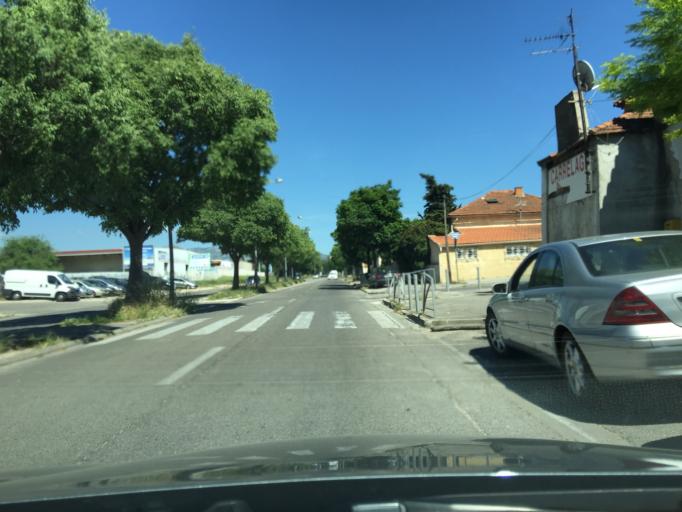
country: FR
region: Provence-Alpes-Cote d'Azur
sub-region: Departement des Bouches-du-Rhone
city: La Penne-sur-Huveaune
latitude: 43.2833
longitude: 5.5348
